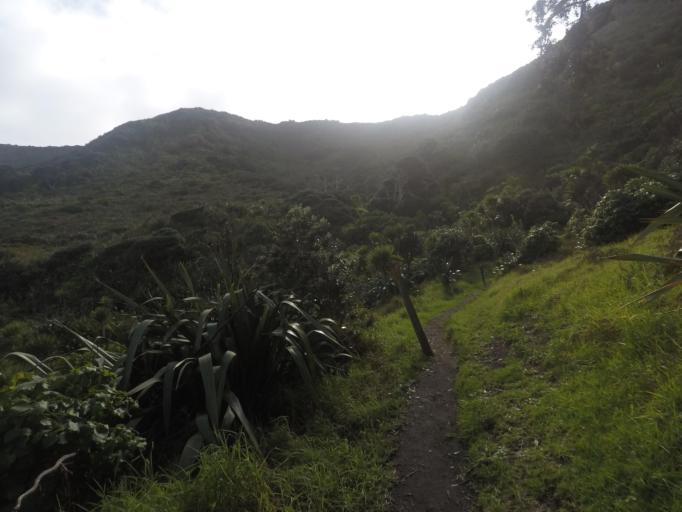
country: NZ
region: Auckland
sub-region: Auckland
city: Muriwai Beach
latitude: -36.8825
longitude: 174.4399
